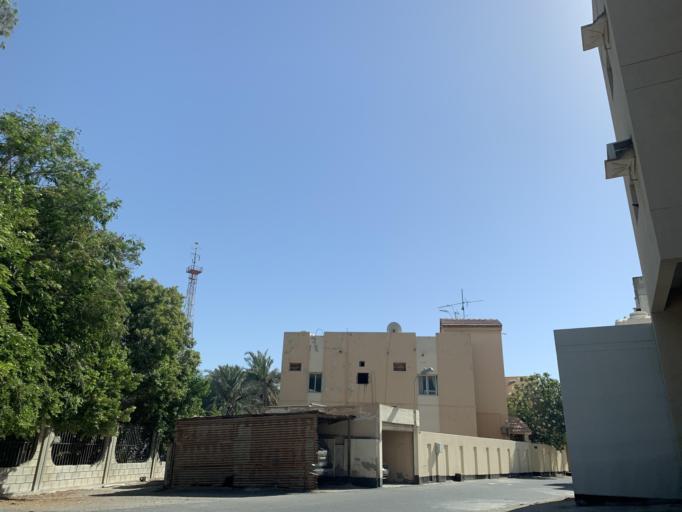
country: BH
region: Manama
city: Jidd Hafs
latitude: 26.2163
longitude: 50.4524
